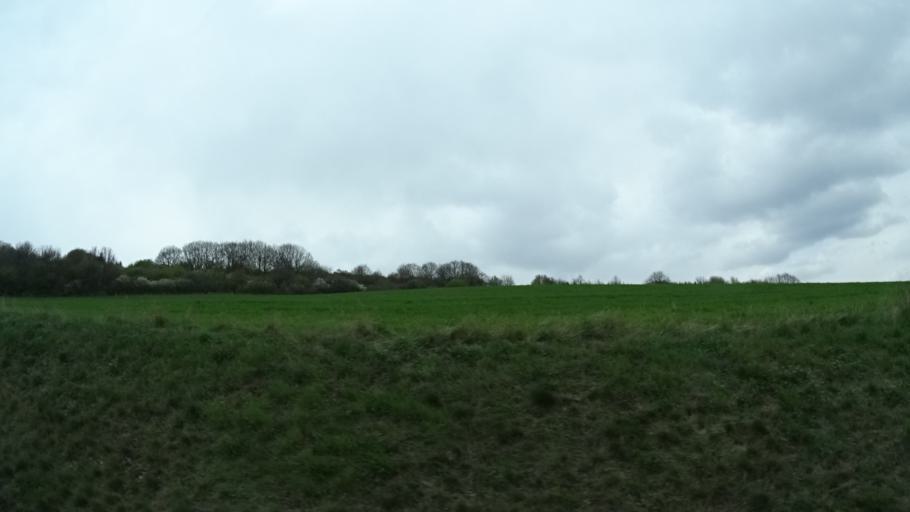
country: DE
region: Rheinland-Pfalz
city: Schwarzerden
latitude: 49.8550
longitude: 7.5151
